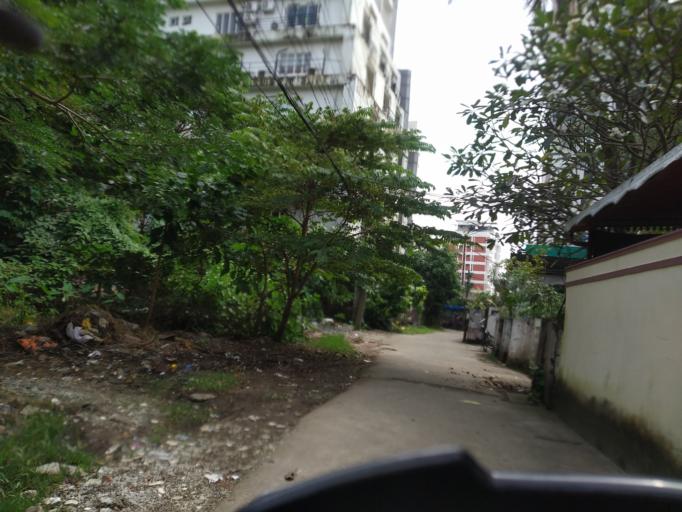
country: IN
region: Kerala
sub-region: Ernakulam
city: Cochin
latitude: 9.9553
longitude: 76.2957
